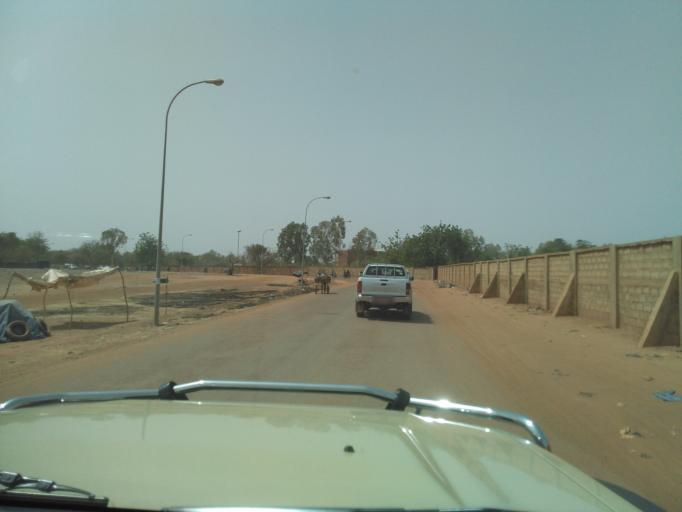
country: BF
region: Centre
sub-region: Kadiogo Province
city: Ouagadougou
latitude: 12.3970
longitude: -1.5581
